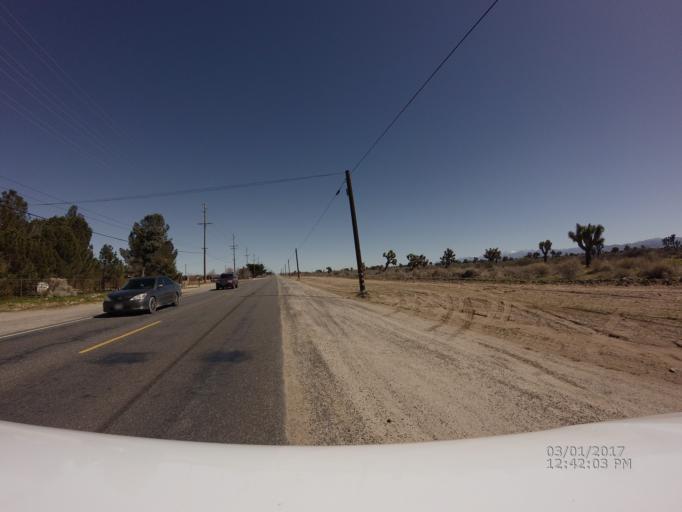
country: US
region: California
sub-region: Los Angeles County
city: Desert View Highlands
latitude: 34.6457
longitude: -118.1601
